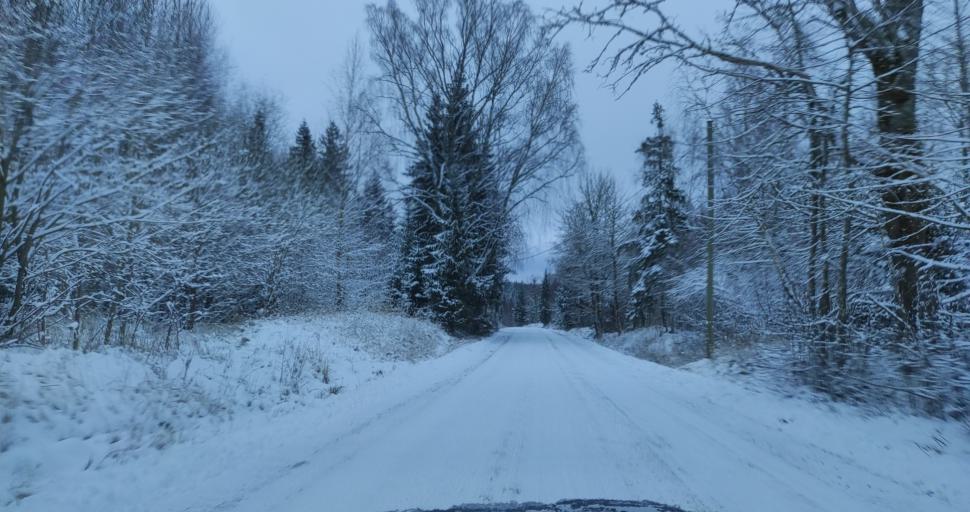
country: LV
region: Kuldigas Rajons
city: Kuldiga
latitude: 56.9498
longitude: 21.7752
